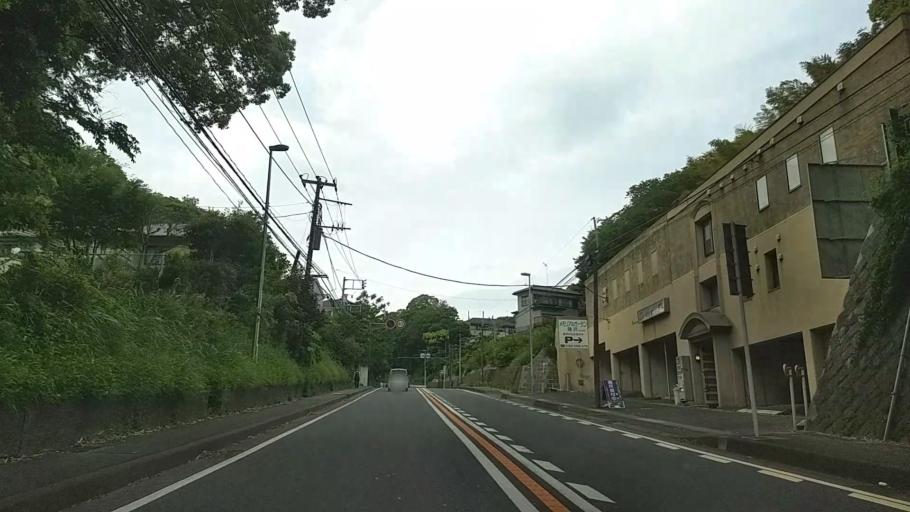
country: JP
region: Kanagawa
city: Fujisawa
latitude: 35.3484
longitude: 139.4894
